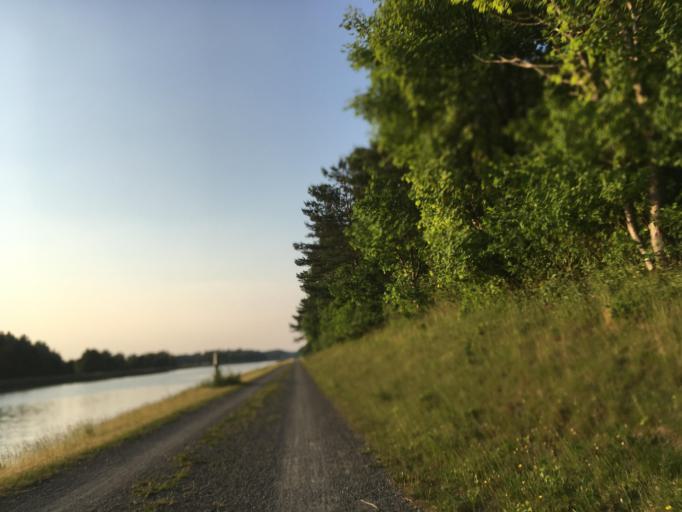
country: DE
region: Lower Saxony
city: Wendisch Evern
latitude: 53.2575
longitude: 10.4861
